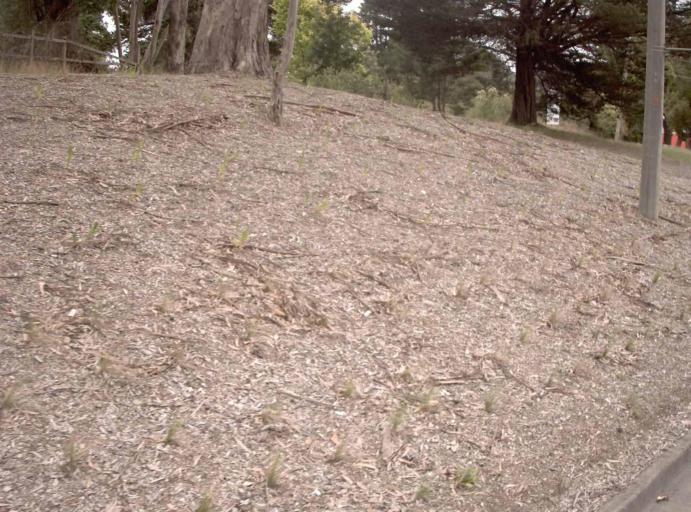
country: AU
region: Victoria
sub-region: Yarra Ranges
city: Lilydale
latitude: -37.7565
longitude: 145.3597
